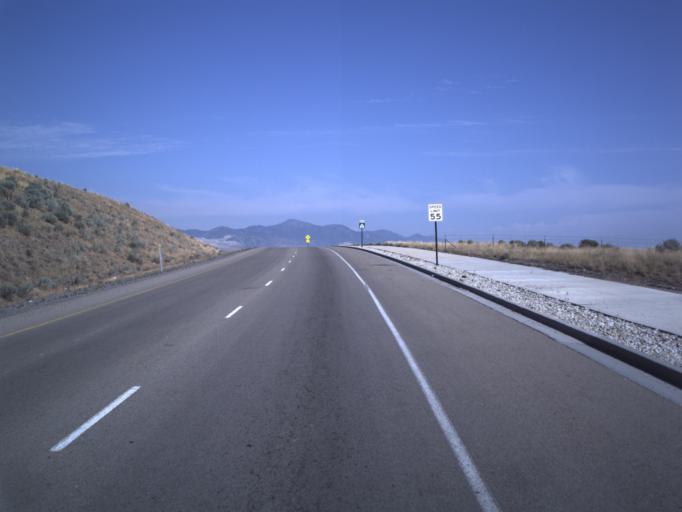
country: US
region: Utah
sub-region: Salt Lake County
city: Bluffdale
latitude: 40.4637
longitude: -111.9535
